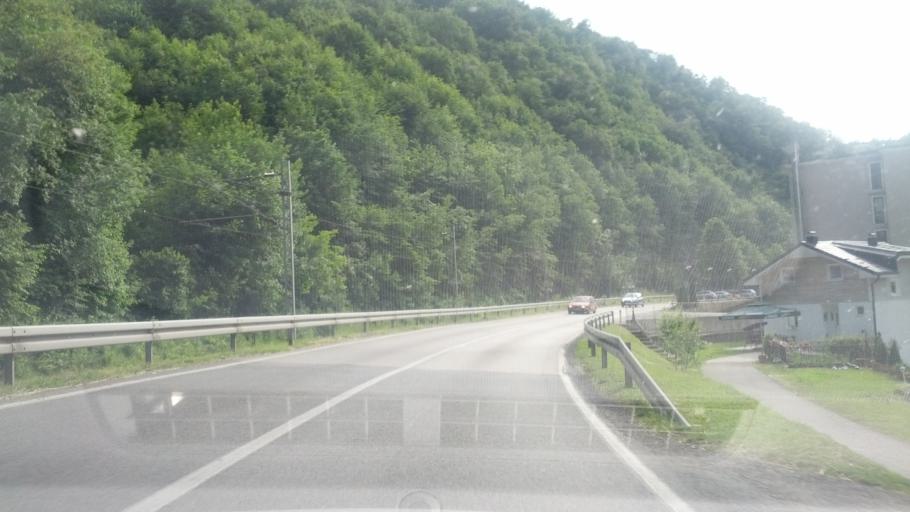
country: BA
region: Federation of Bosnia and Herzegovina
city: Ostrozac
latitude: 44.8822
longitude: 15.9018
